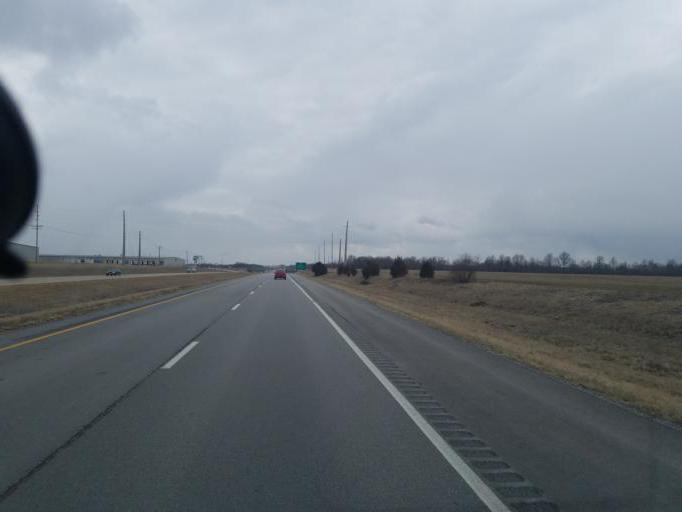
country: US
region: Missouri
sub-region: Randolph County
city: Moberly
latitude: 39.4020
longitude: -92.4128
